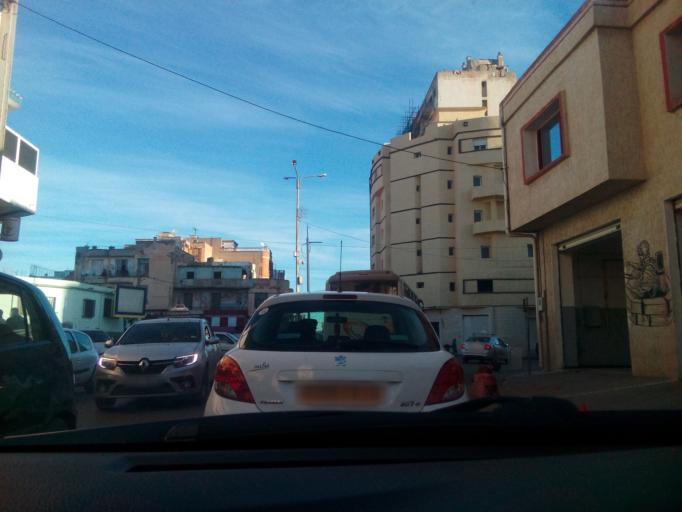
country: DZ
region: Oran
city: Oran
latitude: 35.6866
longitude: -0.6566
